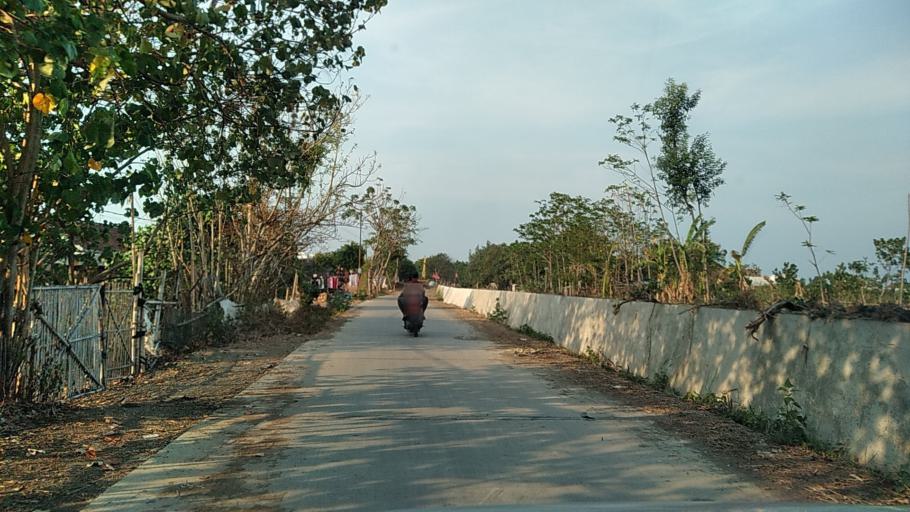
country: ID
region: Central Java
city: Semarang
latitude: -6.9535
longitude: 110.3058
